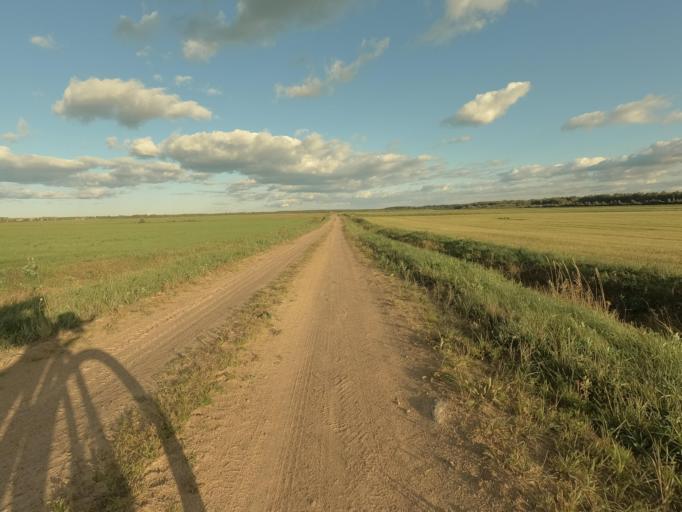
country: RU
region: Leningrad
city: Imeni Sverdlova
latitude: 59.8637
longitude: 30.7419
